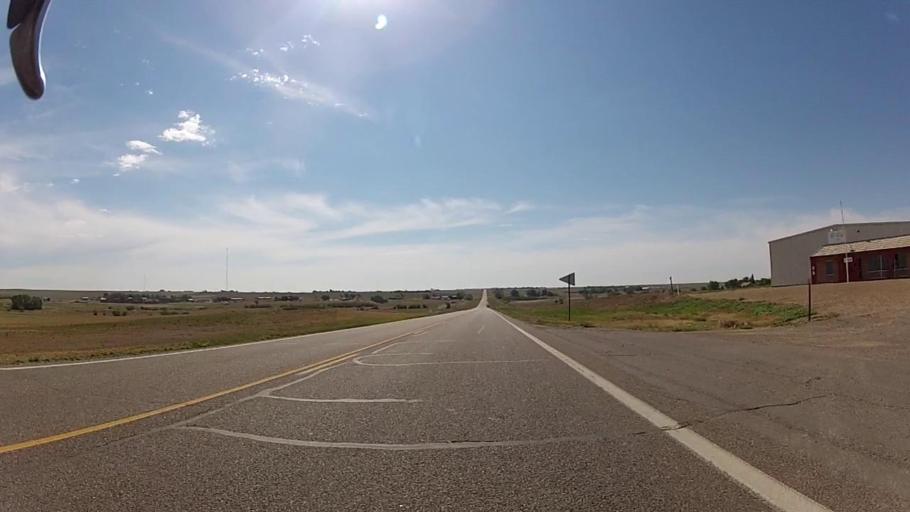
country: US
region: Kansas
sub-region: Grant County
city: Ulysses
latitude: 37.5723
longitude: -101.3363
